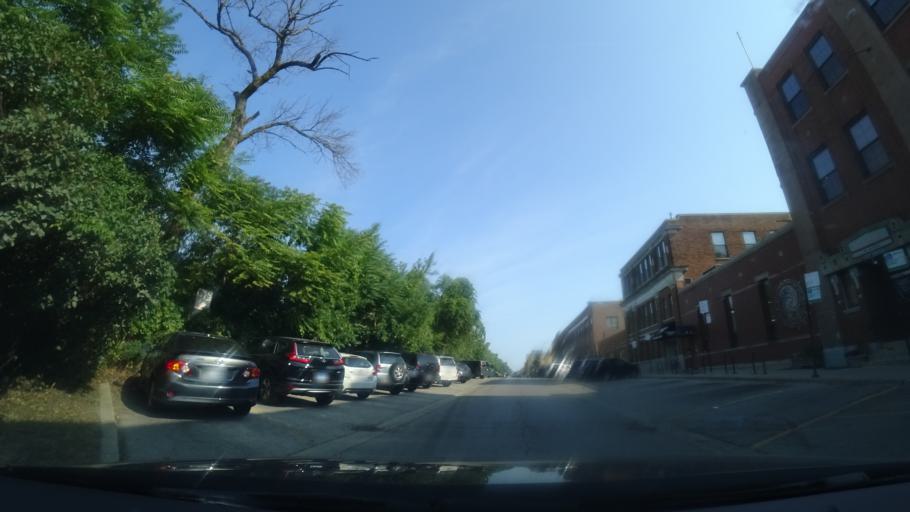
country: US
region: Illinois
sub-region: Cook County
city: Lincolnwood
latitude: 41.9617
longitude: -87.6738
